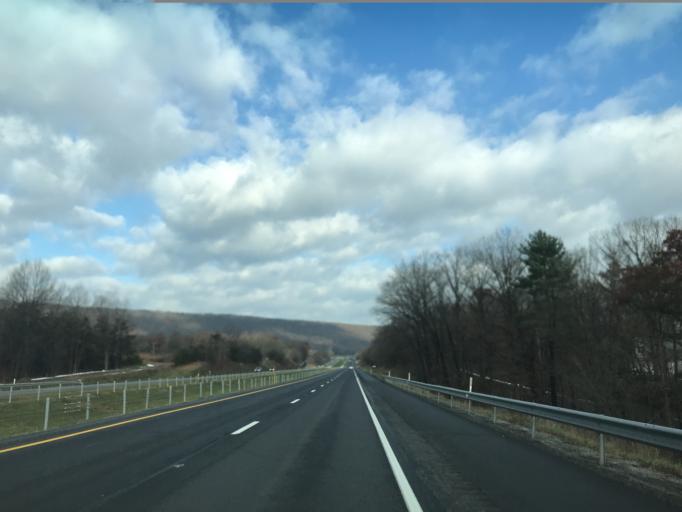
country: US
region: Maryland
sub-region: Washington County
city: Hancock
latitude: 39.8222
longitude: -78.2721
